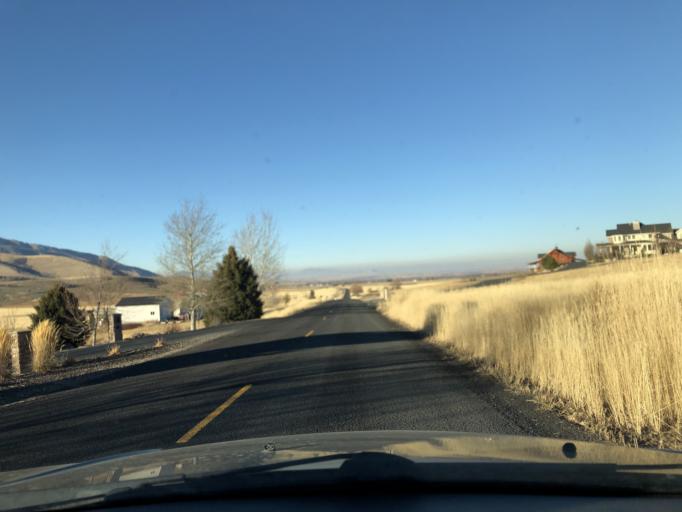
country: US
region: Utah
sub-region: Cache County
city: Wellsville
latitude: 41.5834
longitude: -111.9254
